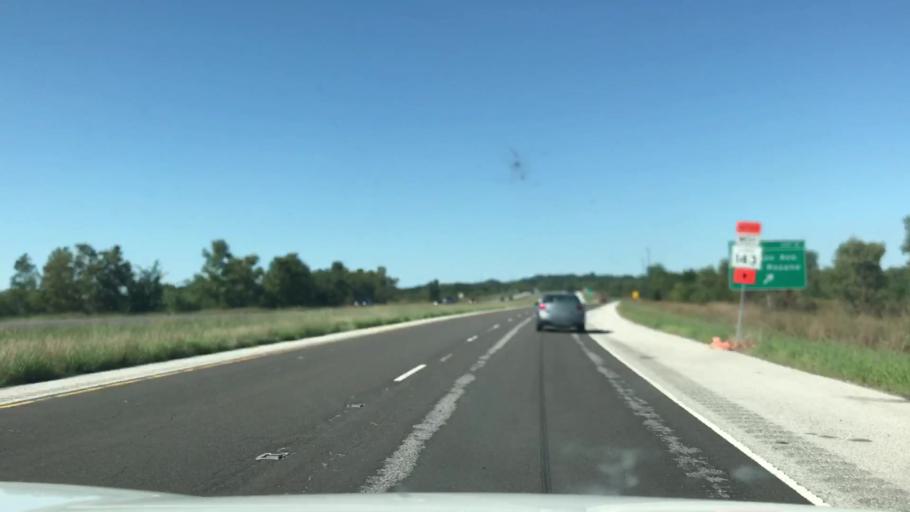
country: US
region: Illinois
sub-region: Madison County
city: South Roxana
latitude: 38.8264
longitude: -90.0435
